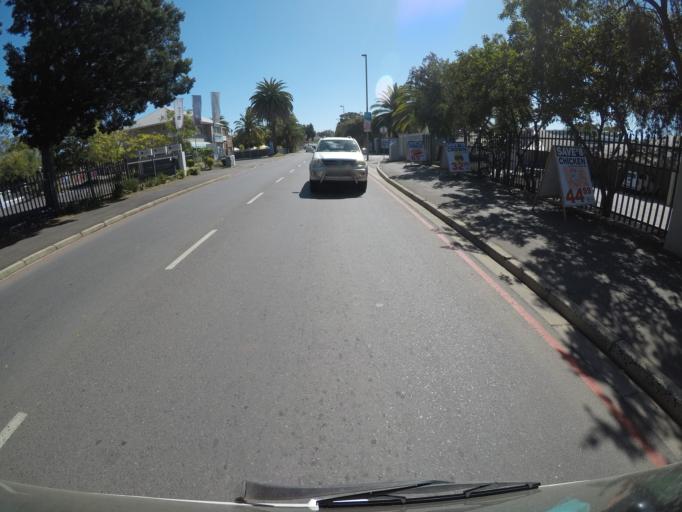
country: ZA
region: Western Cape
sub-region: City of Cape Town
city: Kraaifontein
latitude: -33.8319
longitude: 18.6463
